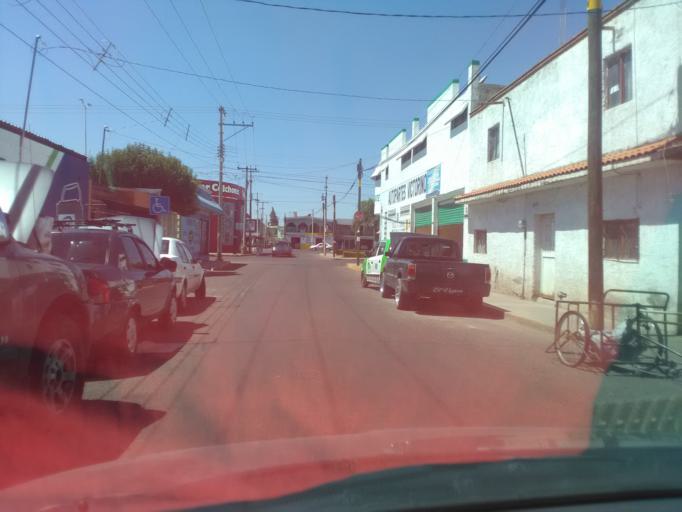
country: MX
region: Durango
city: Victoria de Durango
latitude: 24.0204
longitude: -104.6602
